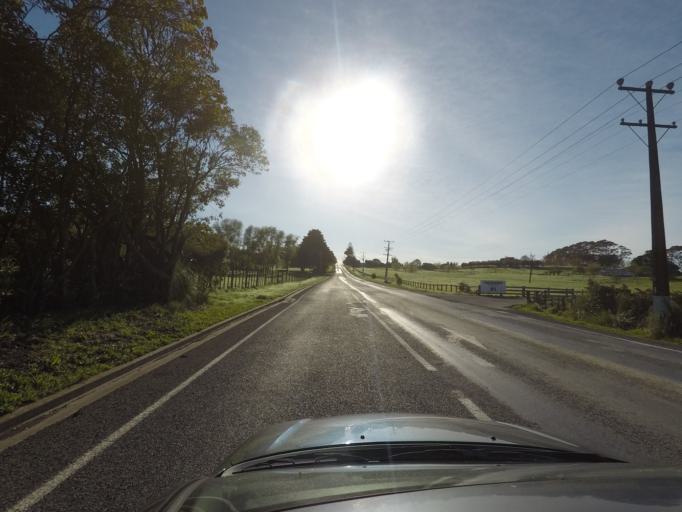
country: NZ
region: Auckland
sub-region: Auckland
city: Red Hill
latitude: -36.9981
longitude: 174.9707
